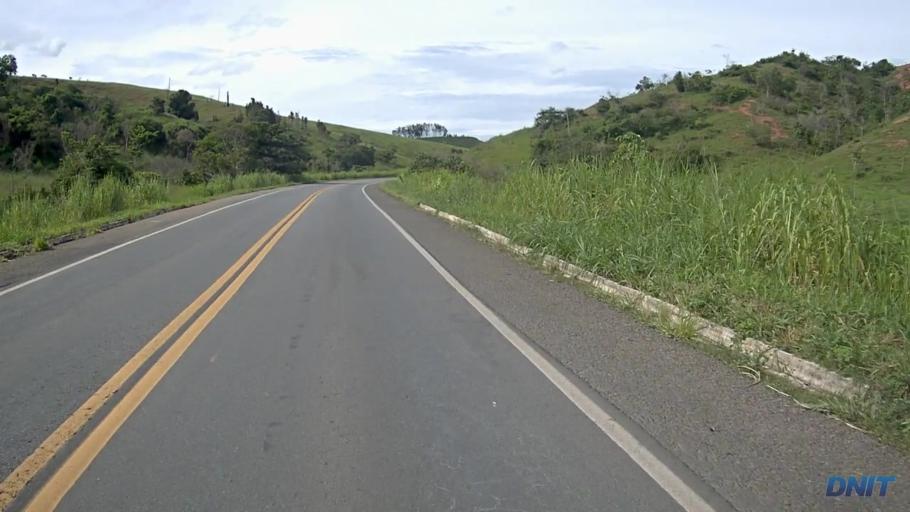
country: BR
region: Minas Gerais
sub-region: Belo Oriente
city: Belo Oriente
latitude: -19.2145
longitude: -42.3065
